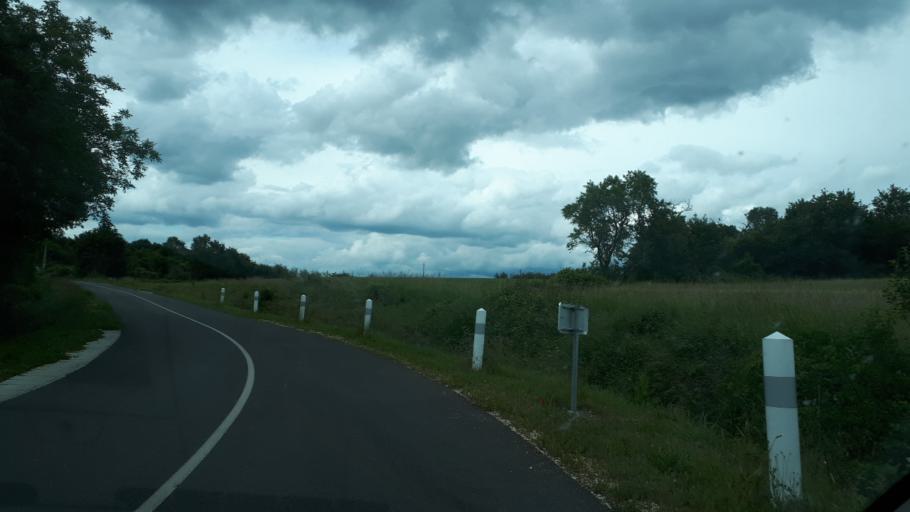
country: FR
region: Centre
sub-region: Departement du Cher
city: Gracay
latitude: 47.1580
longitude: 1.8383
